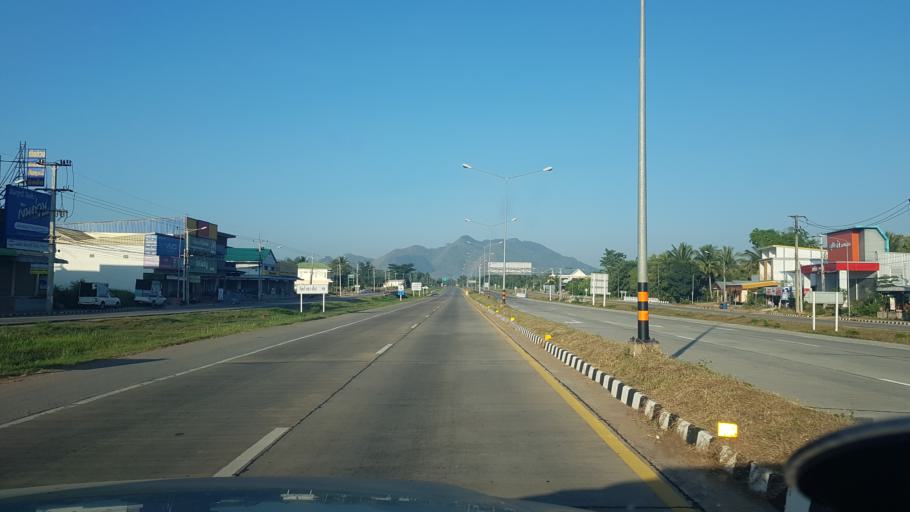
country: TH
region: Chaiyaphum
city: Khon San
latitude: 16.5953
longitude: 101.9269
